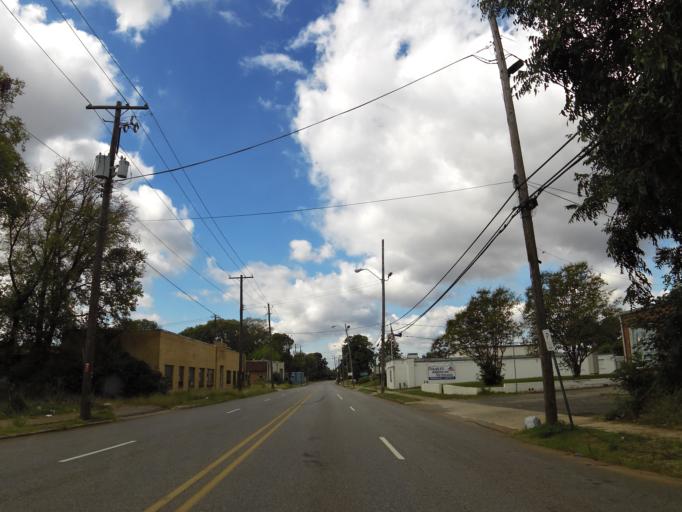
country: US
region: Alabama
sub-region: Jefferson County
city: Birmingham
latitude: 33.5047
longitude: -86.8297
